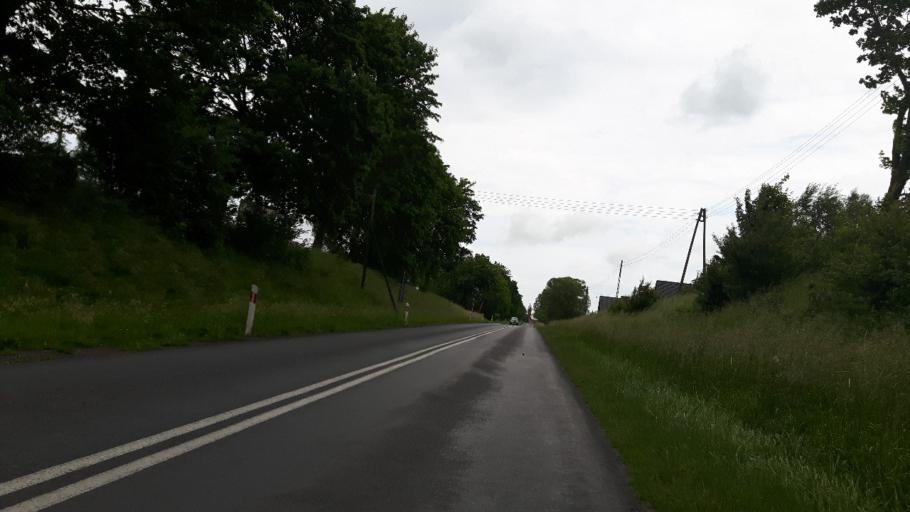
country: PL
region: West Pomeranian Voivodeship
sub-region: Powiat gryficki
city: Gryfice
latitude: 53.9701
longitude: 15.2327
